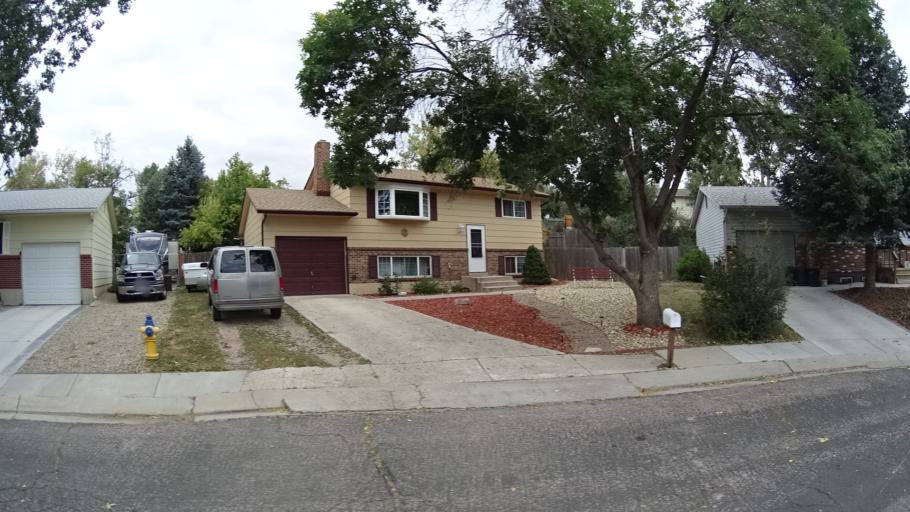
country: US
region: Colorado
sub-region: El Paso County
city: Cimarron Hills
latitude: 38.8925
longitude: -104.7365
